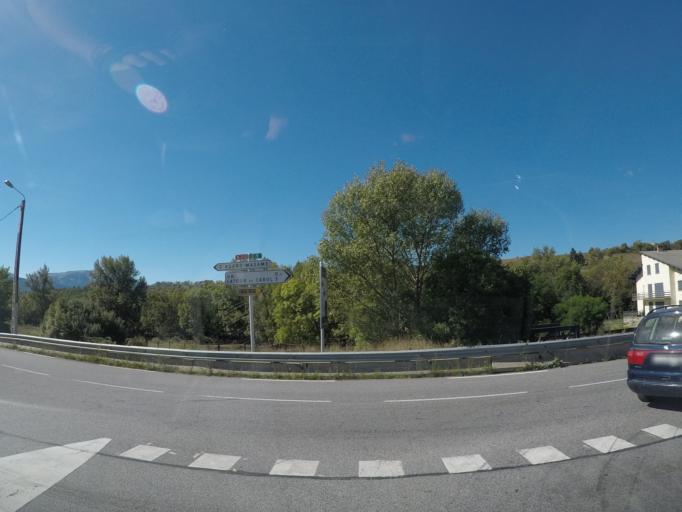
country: FR
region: Languedoc-Roussillon
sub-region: Departement des Pyrenees-Orientales
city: la Guingueta d'Ix
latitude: 42.4599
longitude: 1.9399
